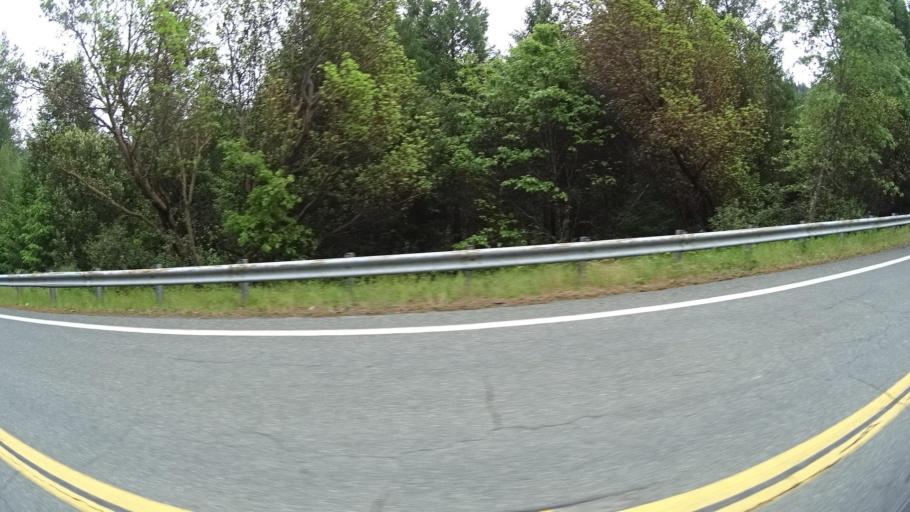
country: US
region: California
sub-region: Humboldt County
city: Willow Creek
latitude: 41.2792
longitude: -123.5873
